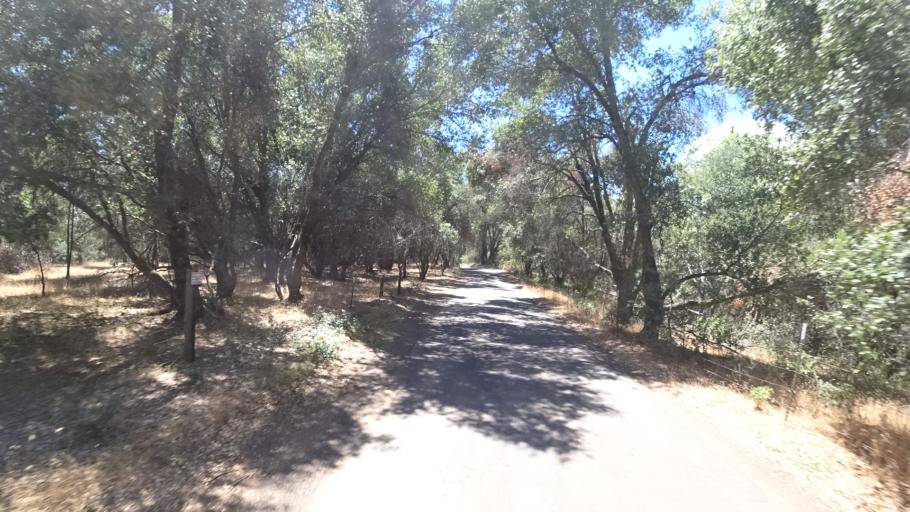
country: US
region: California
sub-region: Calaveras County
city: Forest Meadows
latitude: 38.2231
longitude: -120.4510
